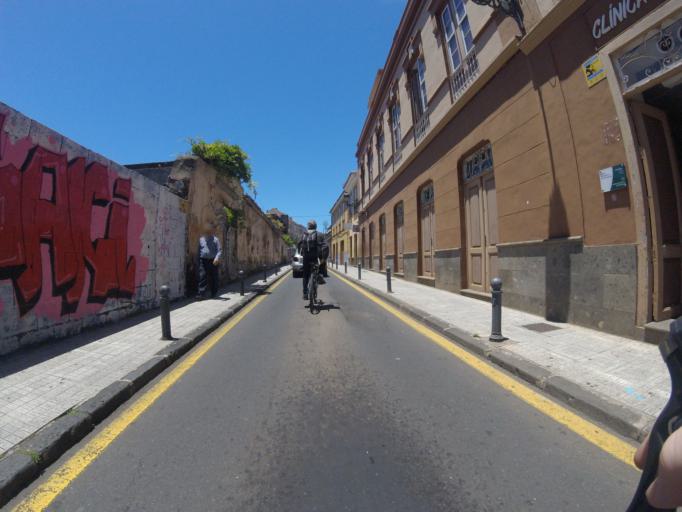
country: ES
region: Canary Islands
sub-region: Provincia de Santa Cruz de Tenerife
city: La Laguna
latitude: 28.4901
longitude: -16.3212
